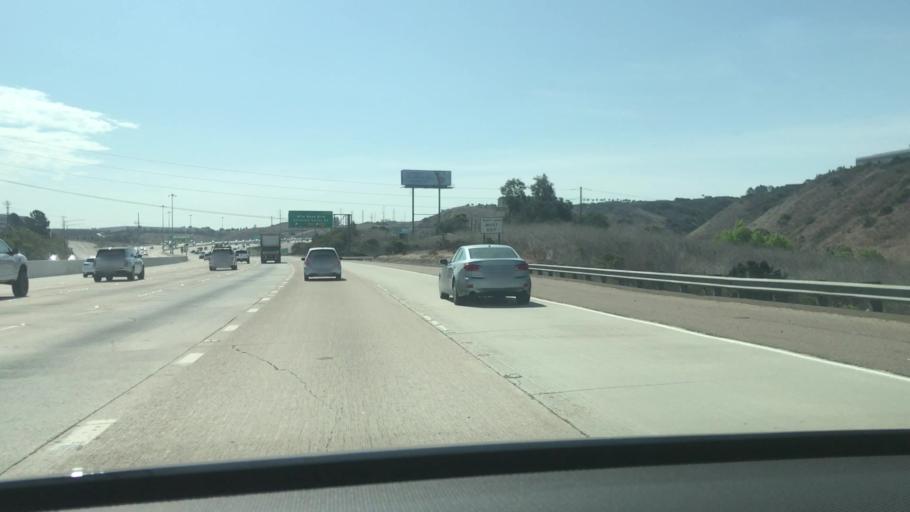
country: US
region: California
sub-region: San Diego County
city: La Jolla
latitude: 32.8941
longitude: -117.2138
